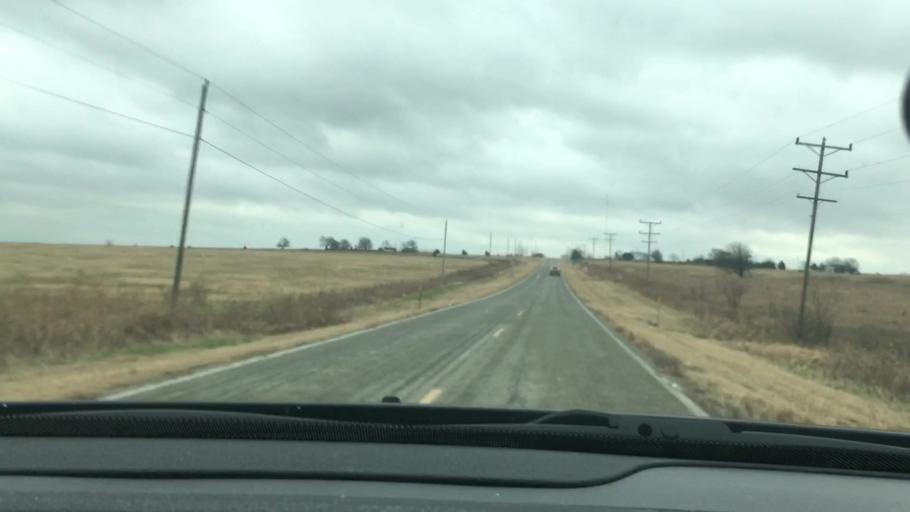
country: US
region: Oklahoma
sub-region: Johnston County
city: Tishomingo
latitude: 34.1433
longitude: -96.5103
